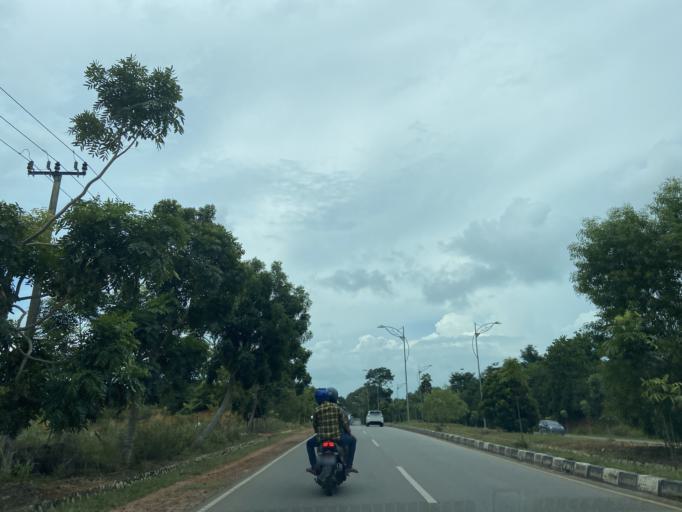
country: SG
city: Singapore
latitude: 1.1447
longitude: 104.1267
